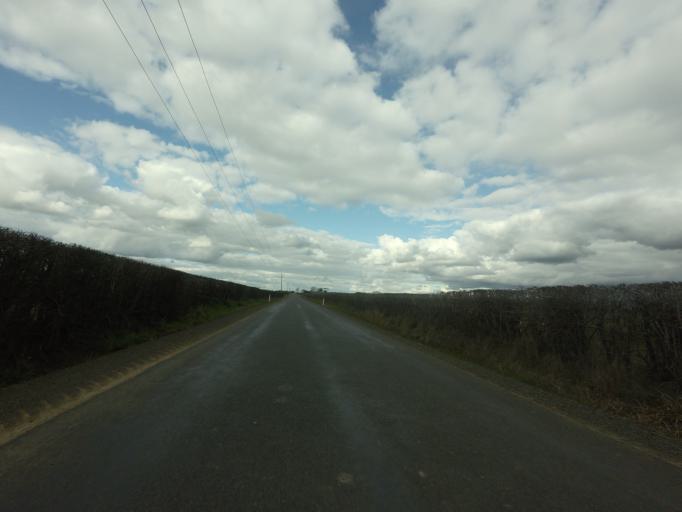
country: AU
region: Tasmania
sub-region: Northern Midlands
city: Longford
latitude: -41.7848
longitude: 147.1009
